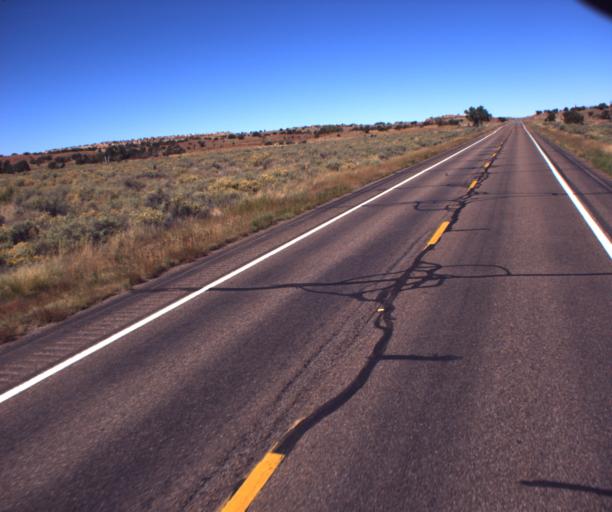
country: US
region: Arizona
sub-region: Apache County
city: Saint Johns
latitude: 34.3834
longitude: -109.4055
